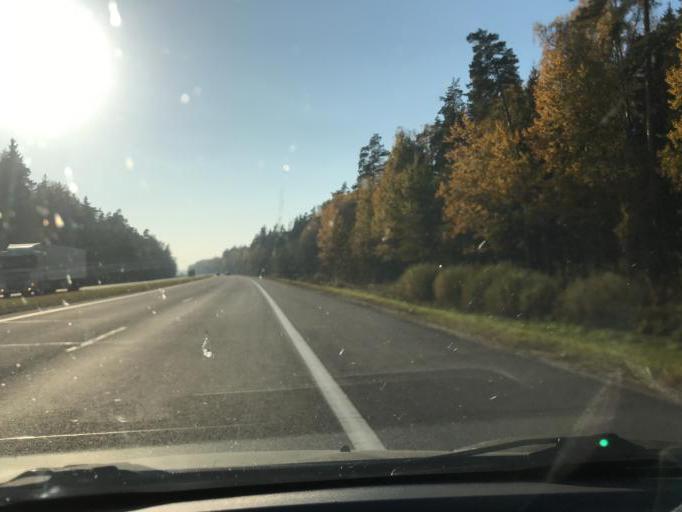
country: BY
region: Minsk
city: Hatava
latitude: 53.7552
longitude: 27.6539
